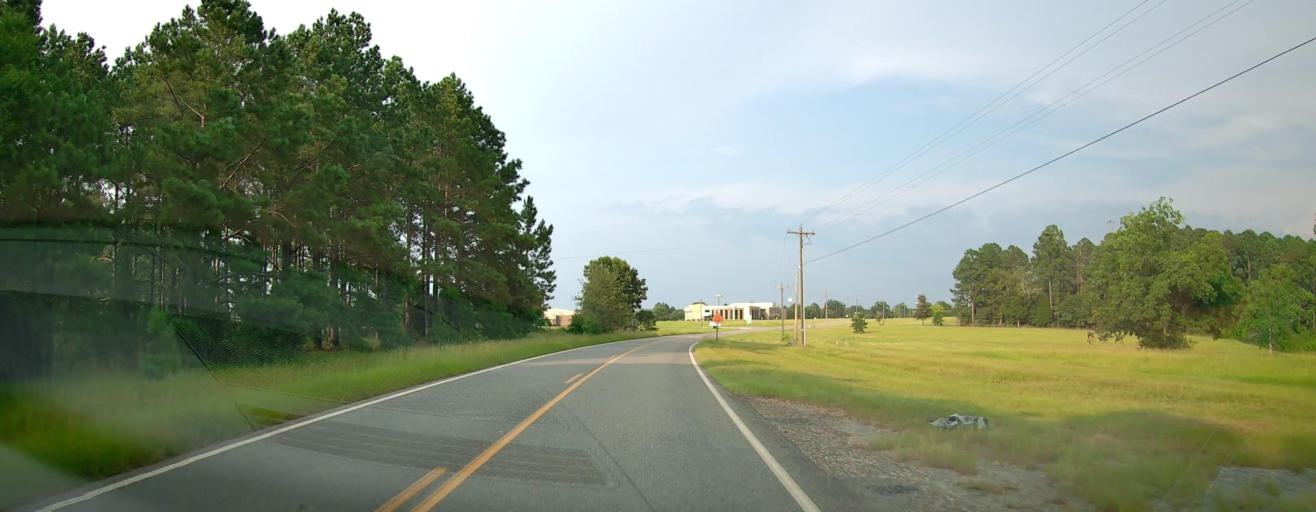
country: US
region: Georgia
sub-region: Laurens County
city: Dublin
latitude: 32.4826
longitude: -82.9483
